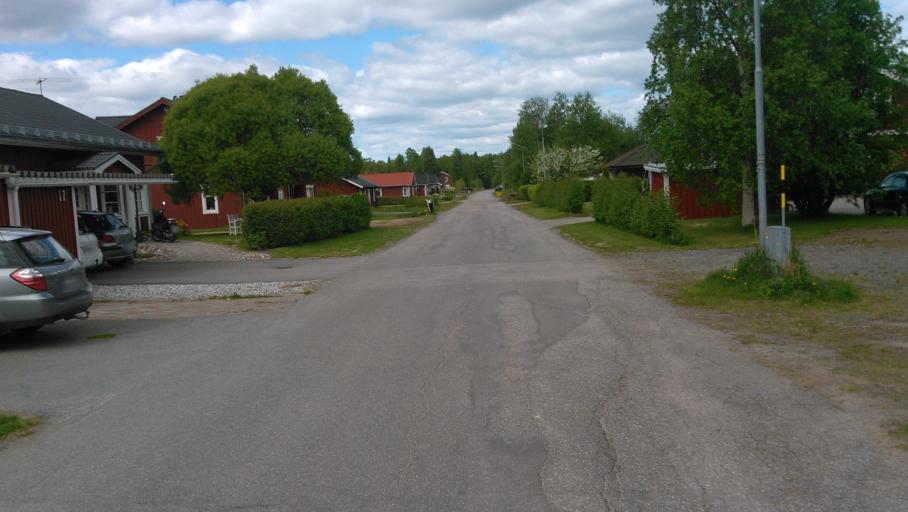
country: SE
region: Vaesterbotten
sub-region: Umea Kommun
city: Roback
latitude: 63.8757
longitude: 20.0567
